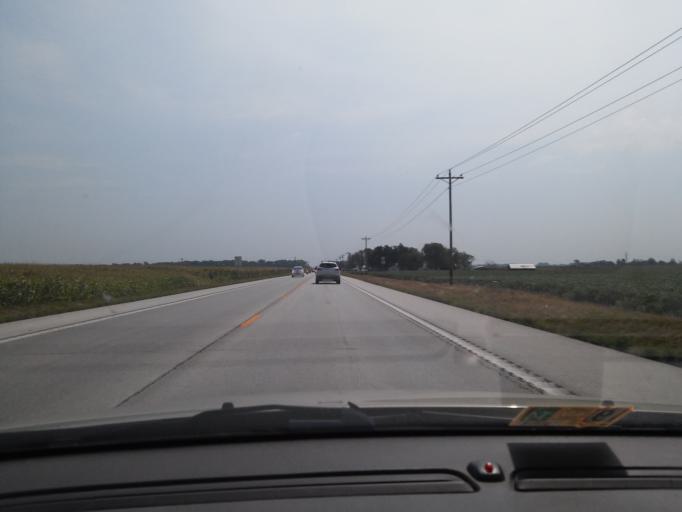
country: US
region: Missouri
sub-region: Audrain County
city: Mexico
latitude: 39.1638
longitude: -91.7665
